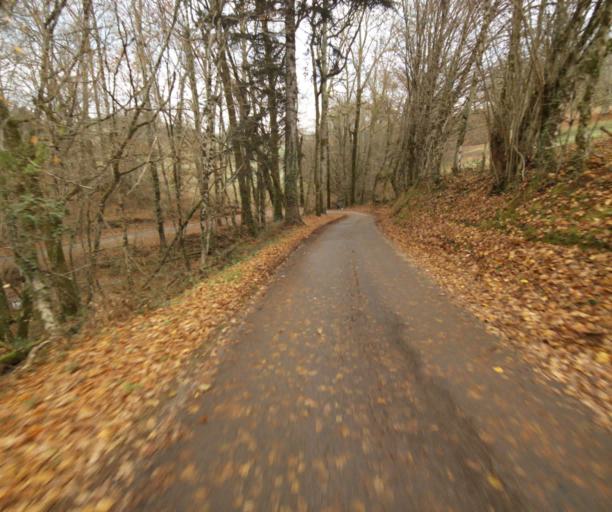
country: FR
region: Limousin
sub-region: Departement de la Correze
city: Sainte-Fortunade
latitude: 45.2346
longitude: 1.7409
